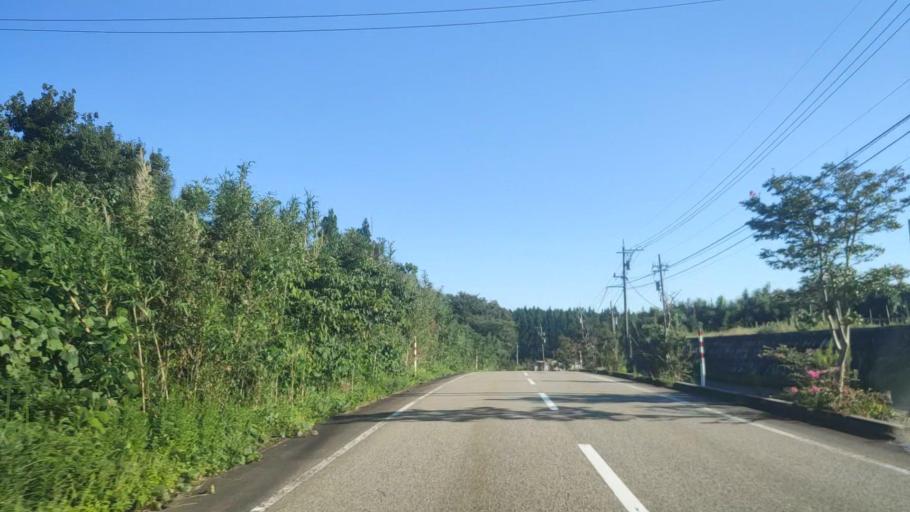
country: JP
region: Ishikawa
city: Nanao
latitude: 37.1294
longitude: 136.9220
